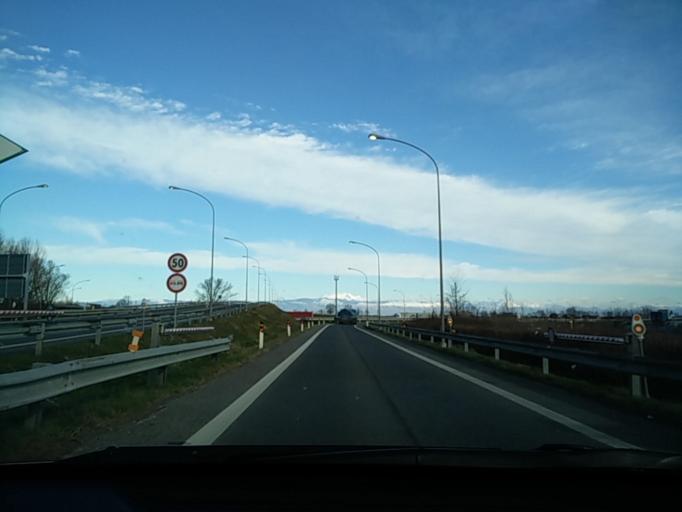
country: IT
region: Veneto
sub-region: Provincia di Venezia
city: Santo Stino di Livenza
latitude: 45.7364
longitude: 12.6867
